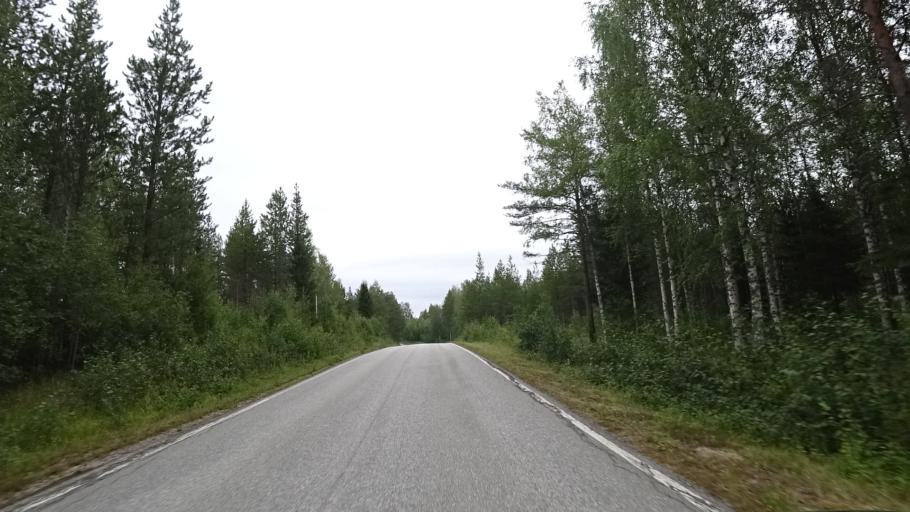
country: FI
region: North Karelia
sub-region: Pielisen Karjala
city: Lieksa
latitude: 63.3726
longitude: 30.3010
